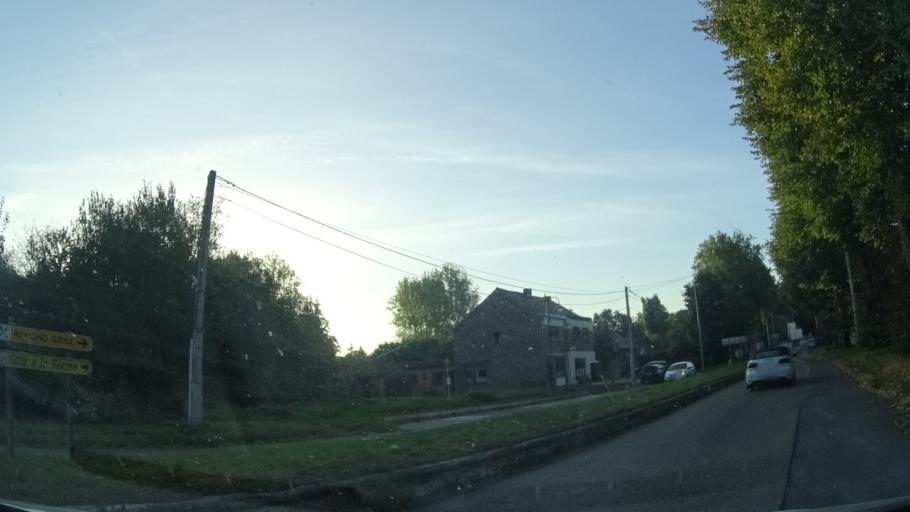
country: BE
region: Wallonia
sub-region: Province du Hainaut
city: Chasse Royale
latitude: 50.4052
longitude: 3.9612
